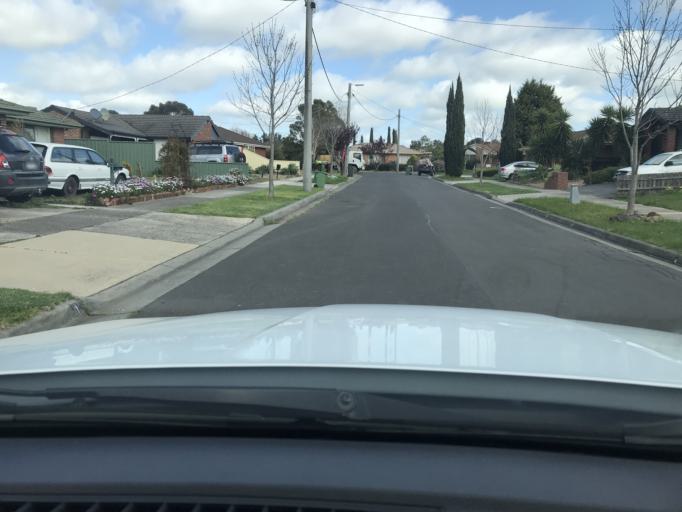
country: AU
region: Victoria
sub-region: Hume
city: Roxburgh Park
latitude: -37.6080
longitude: 144.9269
